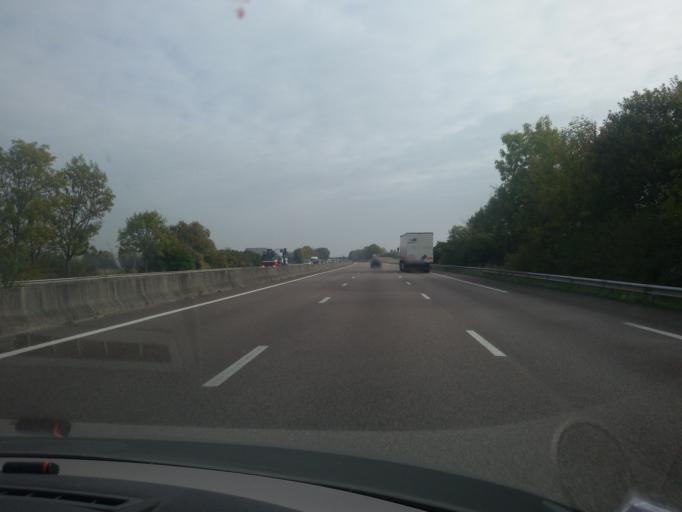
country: FR
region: Haute-Normandie
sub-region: Departement de l'Eure
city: La Chapelle-Reanville
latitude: 49.0822
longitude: 1.3824
